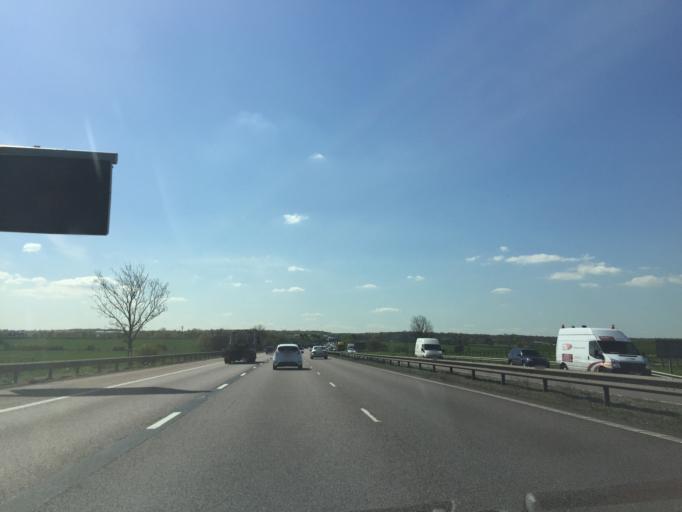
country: GB
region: England
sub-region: Essex
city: Epping
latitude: 51.7322
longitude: 0.1389
